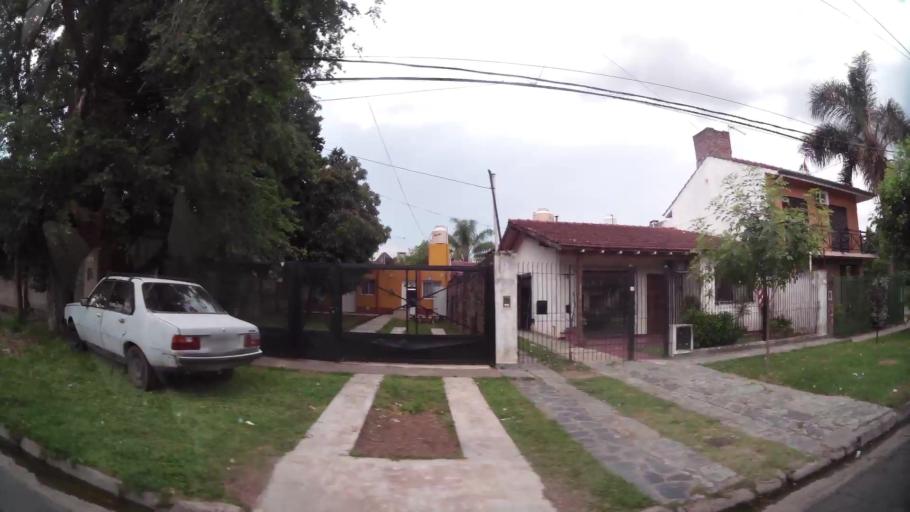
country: AR
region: Buenos Aires
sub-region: Partido de Tigre
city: Tigre
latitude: -34.4742
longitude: -58.6443
